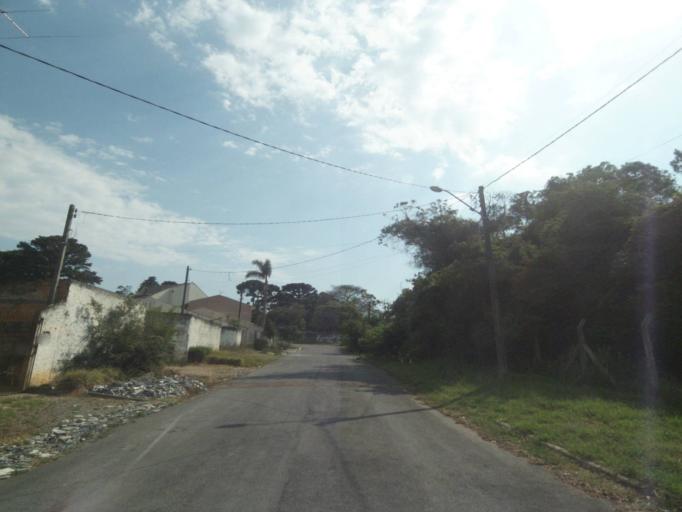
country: BR
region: Parana
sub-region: Sao Jose Dos Pinhais
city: Sao Jose dos Pinhais
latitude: -25.5159
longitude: -49.2521
